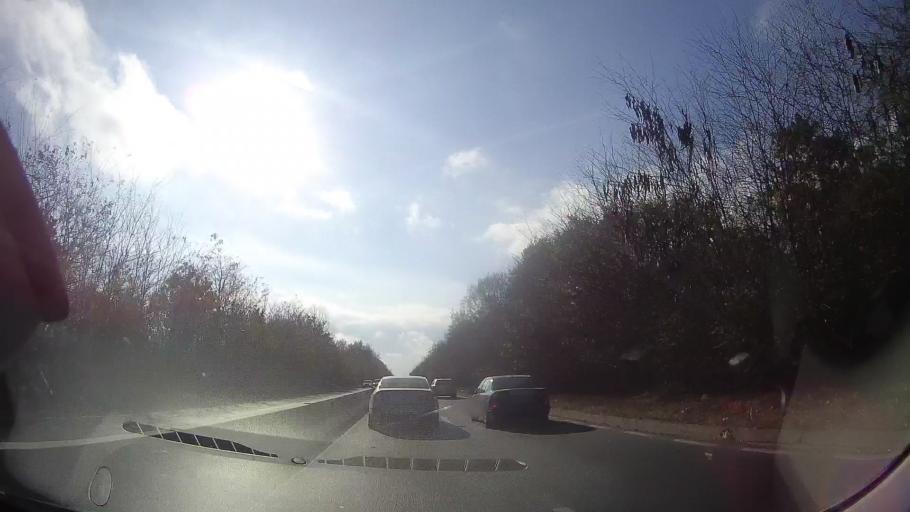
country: RO
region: Constanta
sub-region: Comuna Agigea
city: Agigea
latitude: 44.1292
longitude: 28.6164
